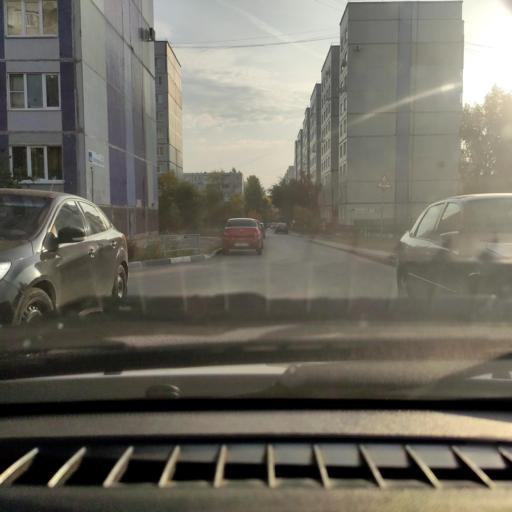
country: RU
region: Samara
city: Zhigulevsk
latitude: 53.4787
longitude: 49.4761
